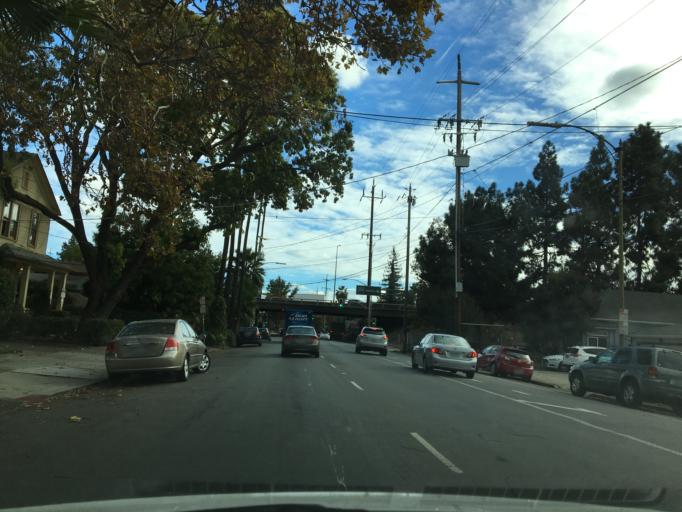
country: US
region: California
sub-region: Santa Clara County
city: San Jose
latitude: 37.3295
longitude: -121.8726
